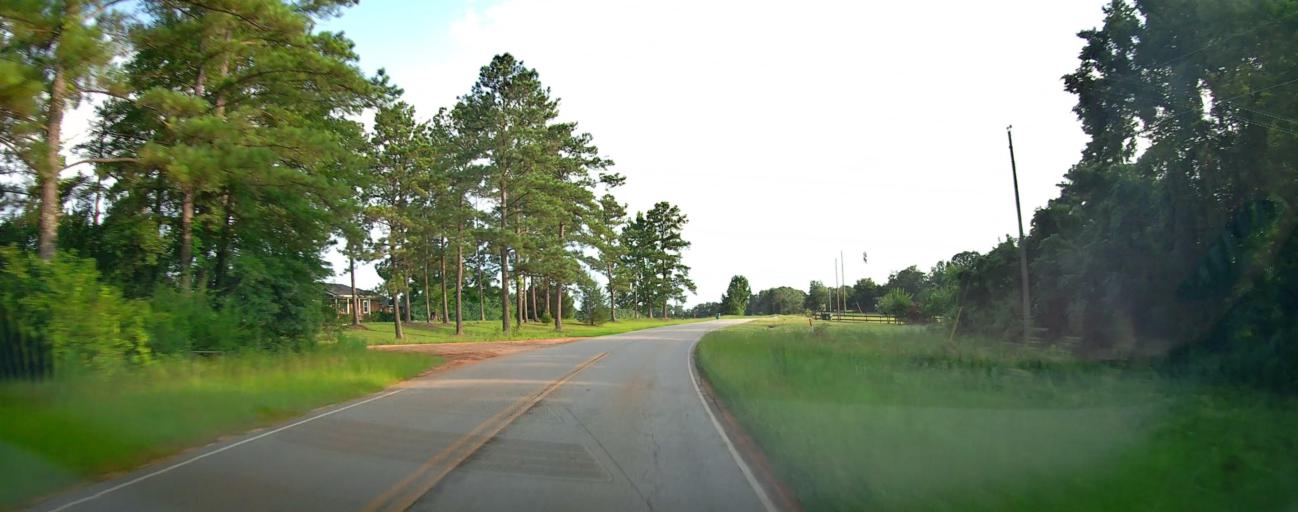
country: US
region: Georgia
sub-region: Peach County
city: Byron
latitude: 32.6937
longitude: -83.8519
